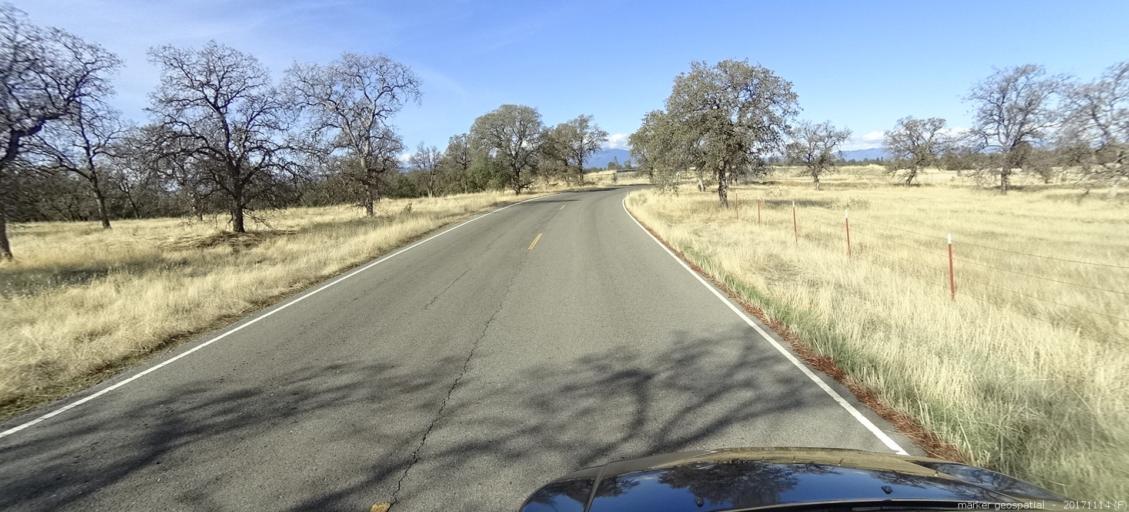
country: US
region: California
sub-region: Shasta County
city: Anderson
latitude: 40.4185
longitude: -122.3654
